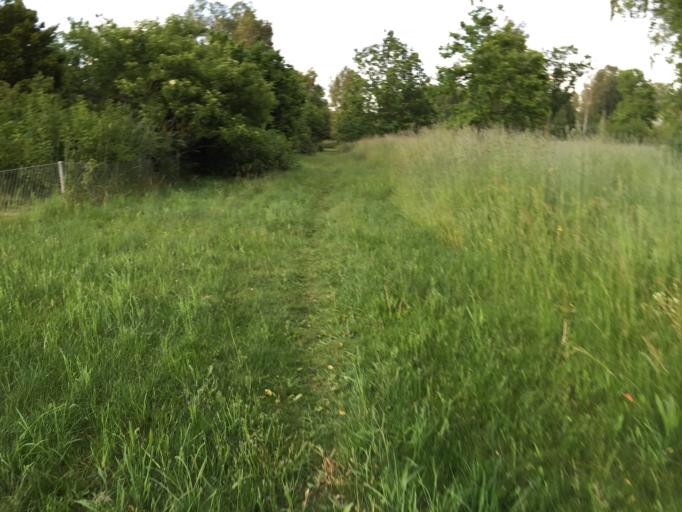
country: SE
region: Skane
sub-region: Lunds Kommun
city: Veberod
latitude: 55.6379
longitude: 13.5077
